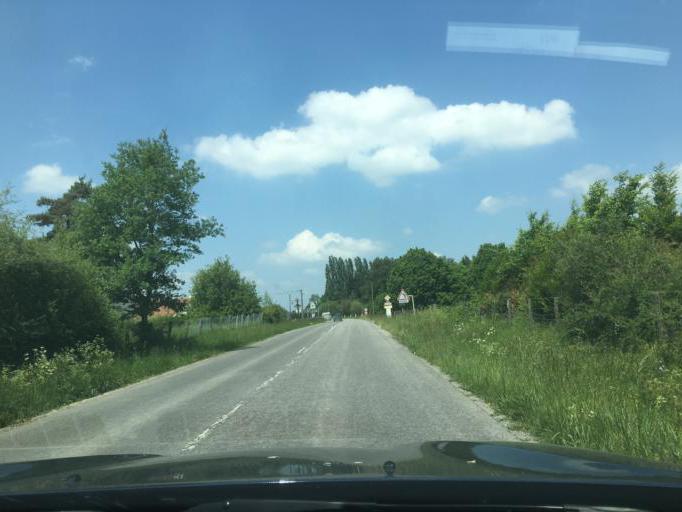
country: FR
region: Centre
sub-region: Departement du Loiret
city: Trainou
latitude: 47.9684
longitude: 2.1127
